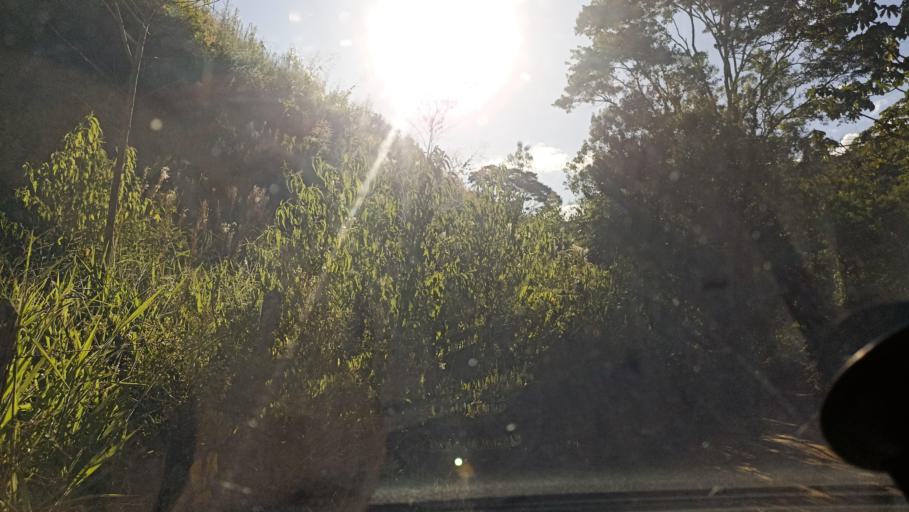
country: BR
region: Minas Gerais
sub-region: Ouro Preto
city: Ouro Preto
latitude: -20.2939
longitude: -43.5684
